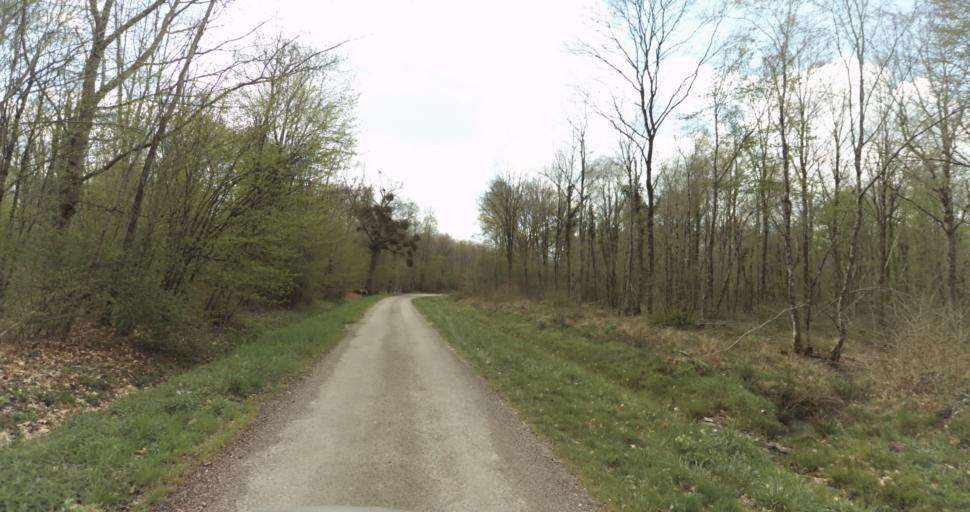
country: FR
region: Franche-Comte
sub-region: Departement du Jura
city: Champvans
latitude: 47.1651
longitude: 5.4457
